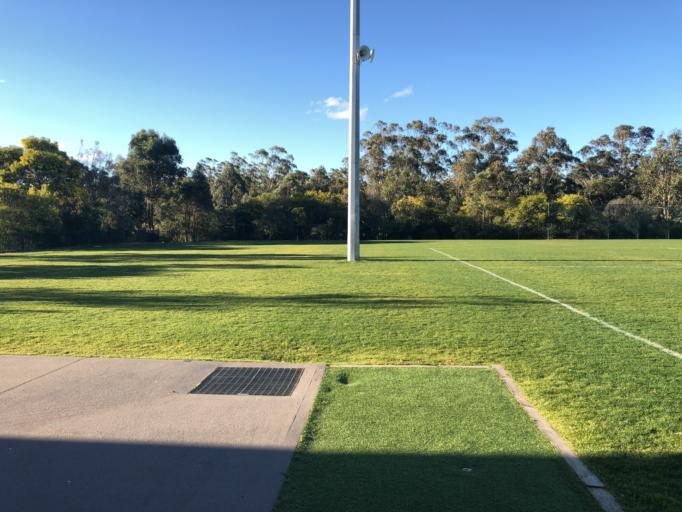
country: AU
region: New South Wales
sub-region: The Hills Shire
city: Glenhaven
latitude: -33.6857
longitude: 151.0151
